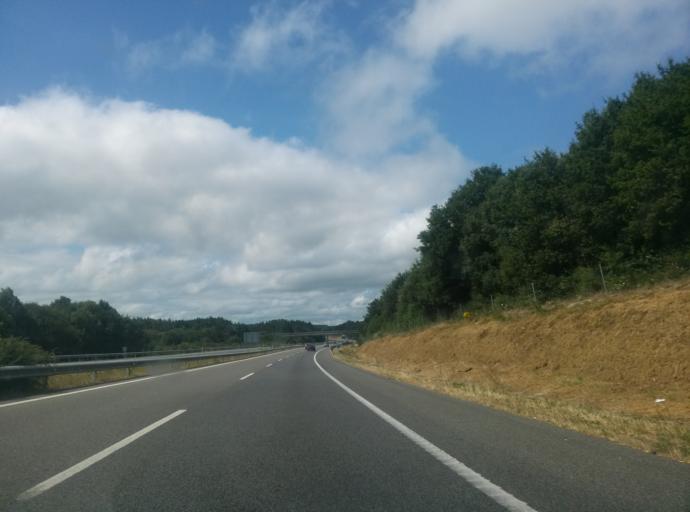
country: ES
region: Galicia
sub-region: Provincia de Lugo
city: Outeiro de Rei
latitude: 43.0661
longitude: -7.5710
